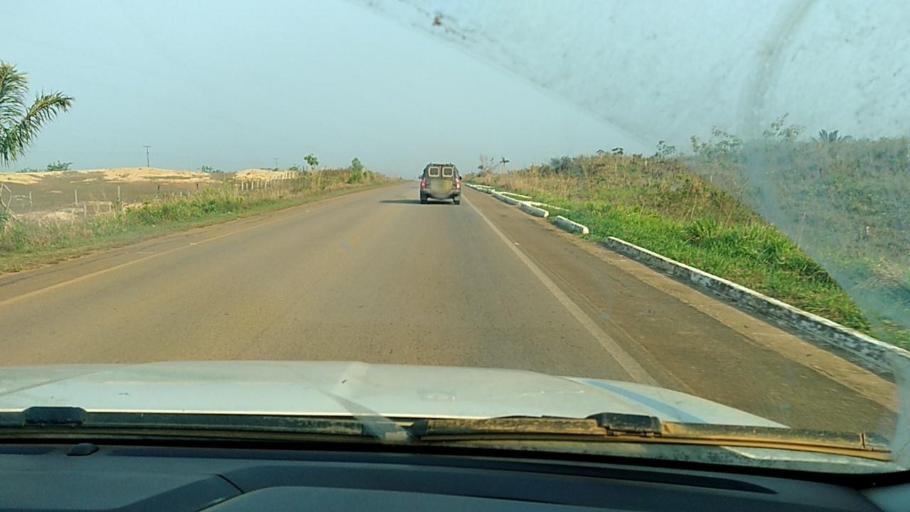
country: BR
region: Rondonia
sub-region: Porto Velho
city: Porto Velho
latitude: -8.7400
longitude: -63.9534
